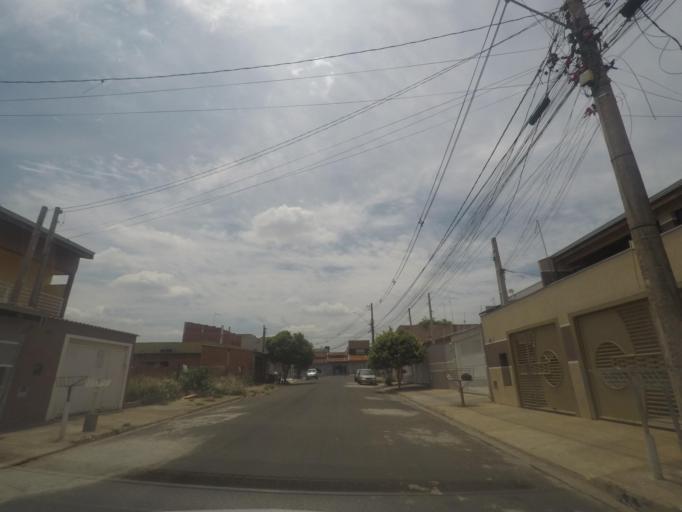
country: BR
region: Sao Paulo
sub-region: Sumare
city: Sumare
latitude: -22.7992
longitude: -47.2692
